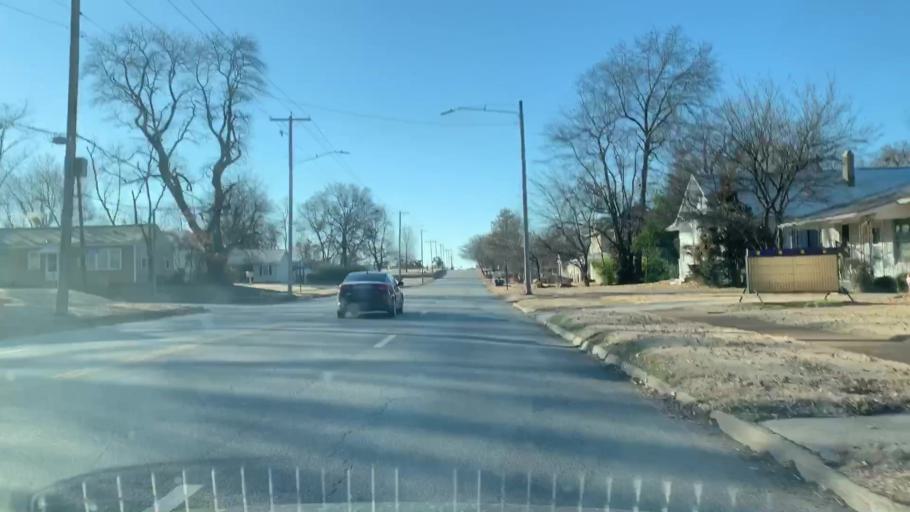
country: US
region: Kansas
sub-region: Crawford County
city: Pittsburg
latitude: 37.3877
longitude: -94.7052
